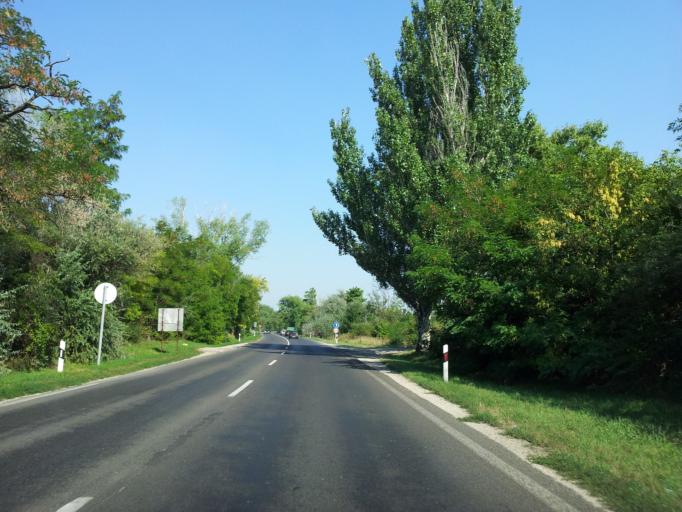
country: HU
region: Somogy
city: Balatonszabadi
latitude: 46.9293
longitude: 18.1288
